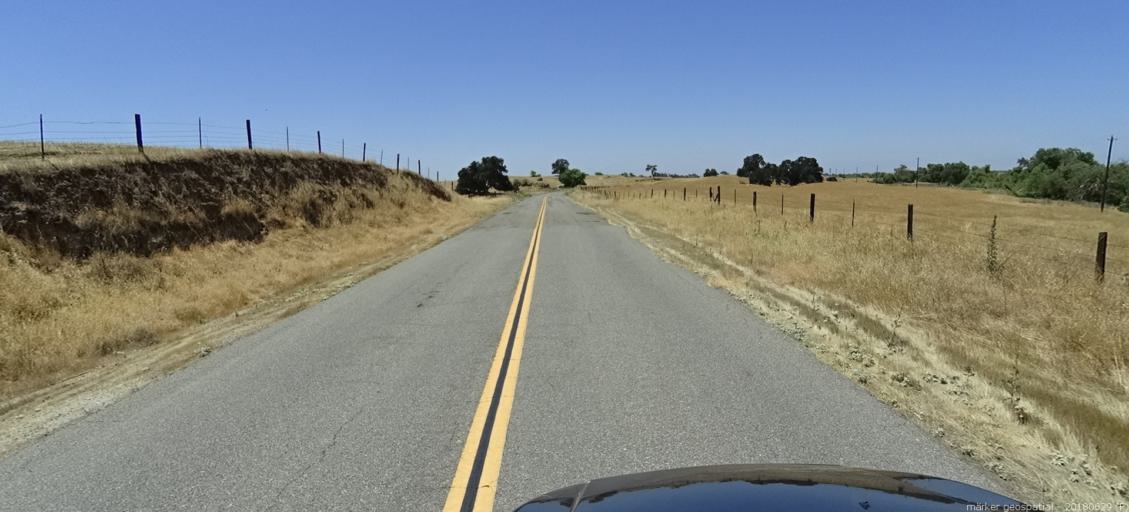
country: US
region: California
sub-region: Madera County
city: Bonadelle Ranchos-Madera Ranchos
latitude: 37.0748
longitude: -119.9008
